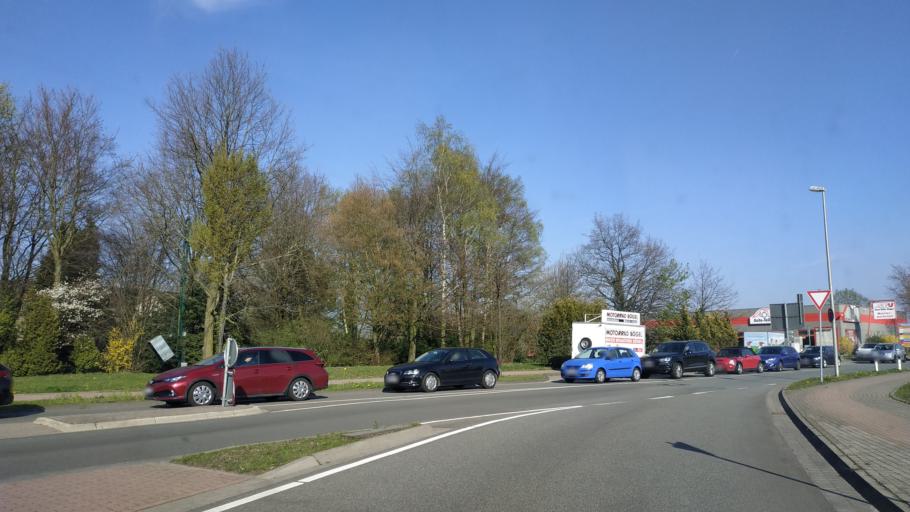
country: DE
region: North Rhine-Westphalia
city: Ibbenburen
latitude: 52.2599
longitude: 7.7138
